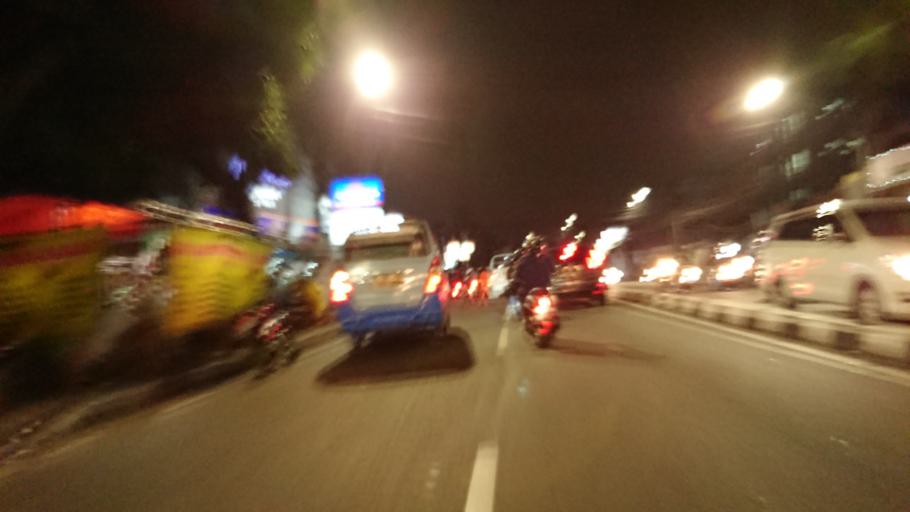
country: ID
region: Jakarta Raya
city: Jakarta
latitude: -6.1920
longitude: 106.8057
